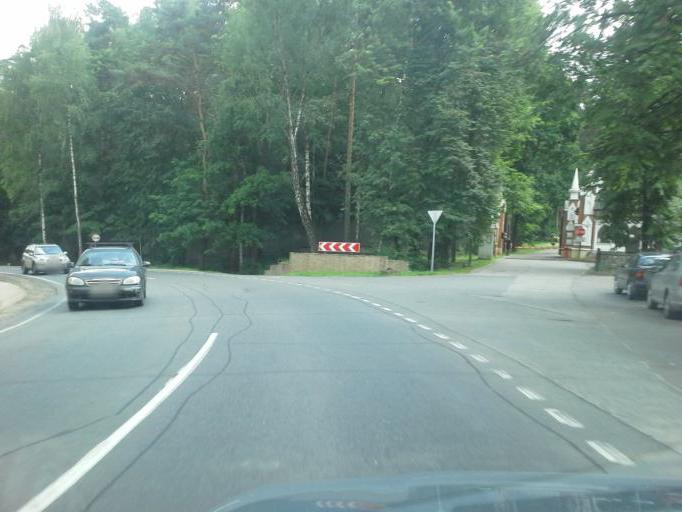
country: RU
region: Moskovskaya
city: Barvikha
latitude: 55.7313
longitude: 37.2726
